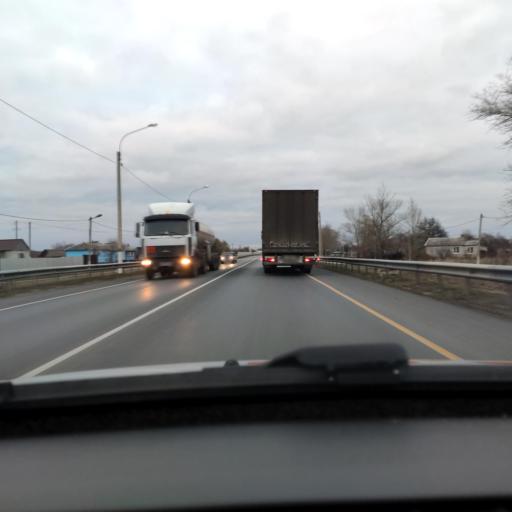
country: RU
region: Lipetsk
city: Khlevnoye
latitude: 52.2620
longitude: 39.1558
